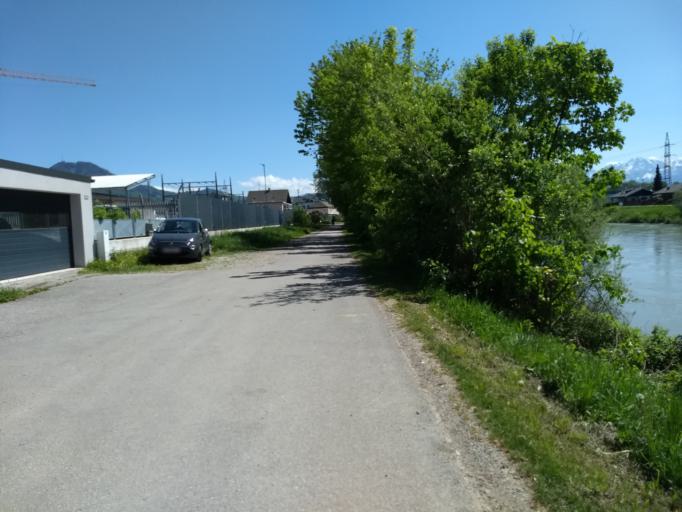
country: AT
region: Salzburg
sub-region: Politischer Bezirk Salzburg-Umgebung
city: Bergheim
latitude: 47.8346
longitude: 13.0254
